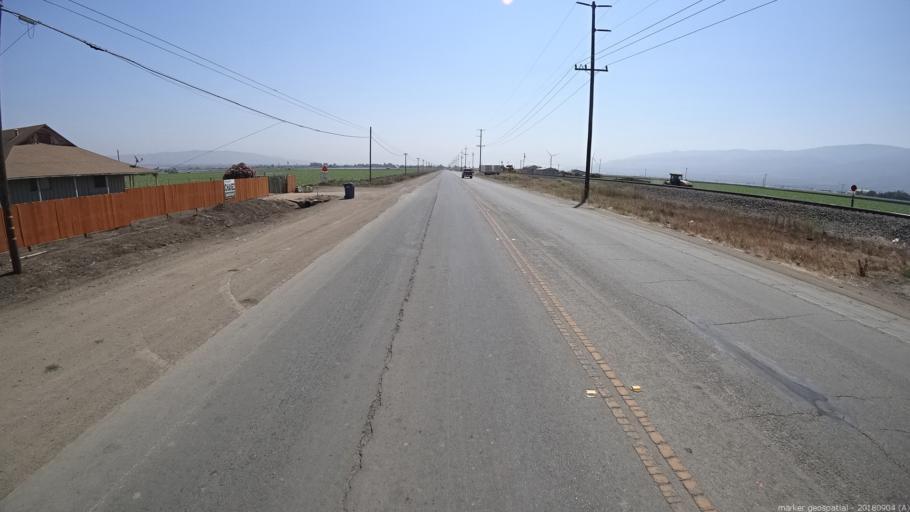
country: US
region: California
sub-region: Monterey County
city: Gonzales
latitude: 36.5200
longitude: -121.4615
